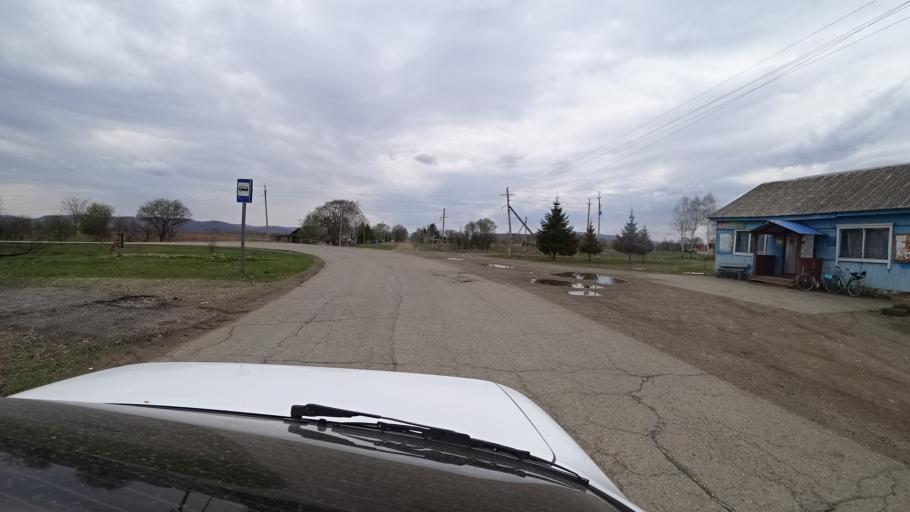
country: RU
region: Primorskiy
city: Novopokrovka
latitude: 45.5779
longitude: 134.3129
